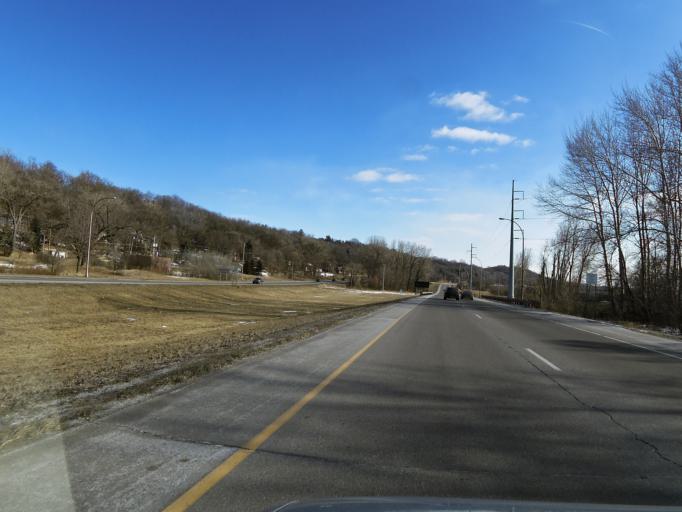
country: US
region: Minnesota
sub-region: Ramsey County
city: Maplewood
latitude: 44.9278
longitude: -93.0224
